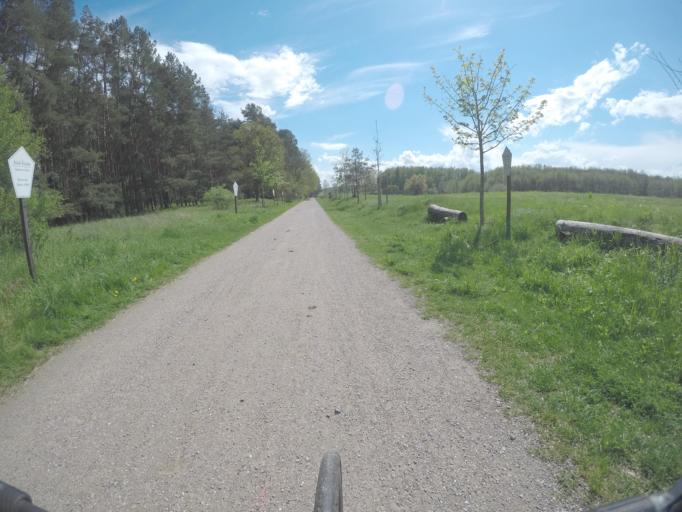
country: DE
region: Brandenburg
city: Biesenthal
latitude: 52.7587
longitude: 13.6297
